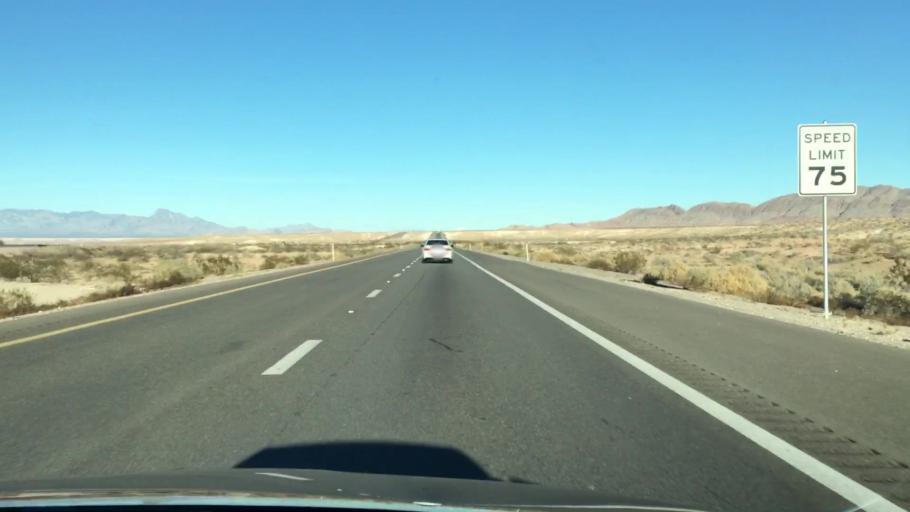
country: US
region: Nevada
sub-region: Clark County
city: Moapa Town
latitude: 36.5579
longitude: -114.6879
